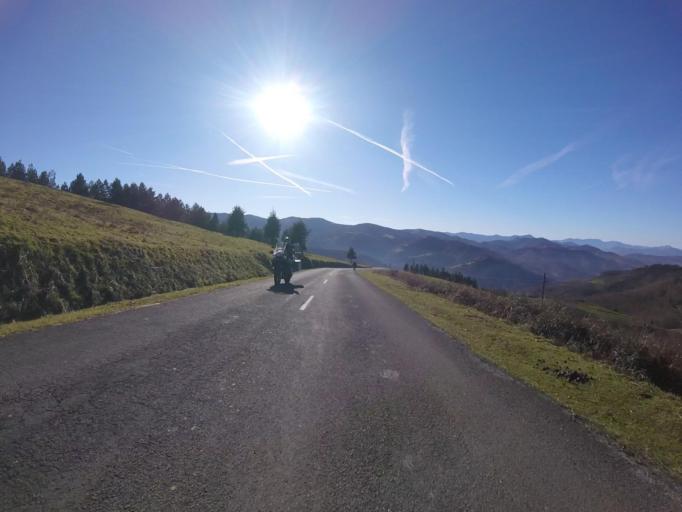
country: ES
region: Basque Country
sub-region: Provincia de Guipuzcoa
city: Irun
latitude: 43.2941
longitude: -1.8070
